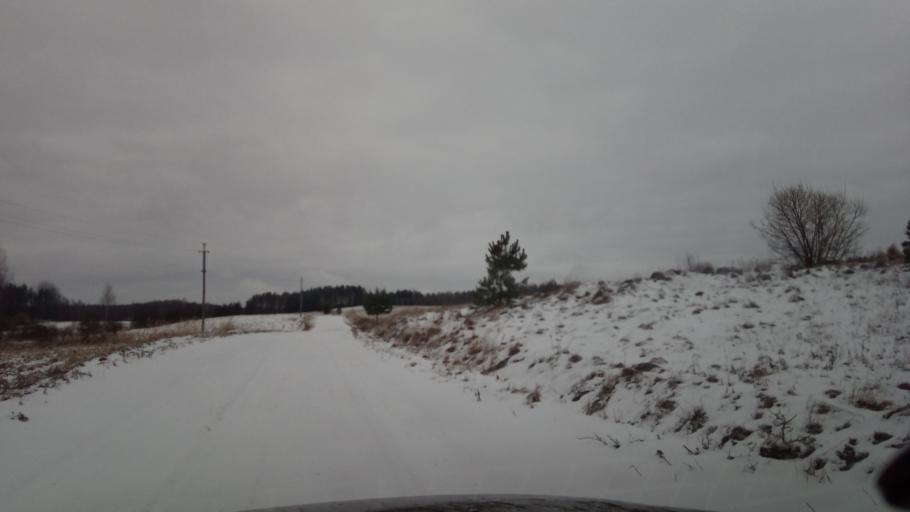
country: LT
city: Zarasai
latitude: 55.6868
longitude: 26.1012
